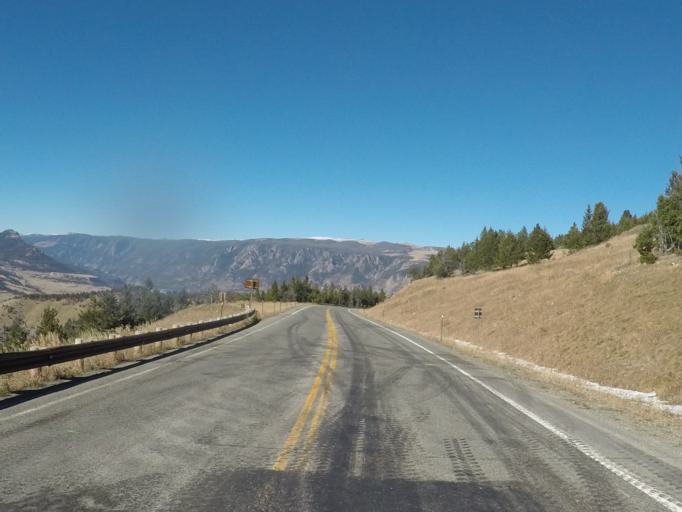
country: US
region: Wyoming
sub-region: Park County
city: Cody
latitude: 44.7462
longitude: -109.3829
